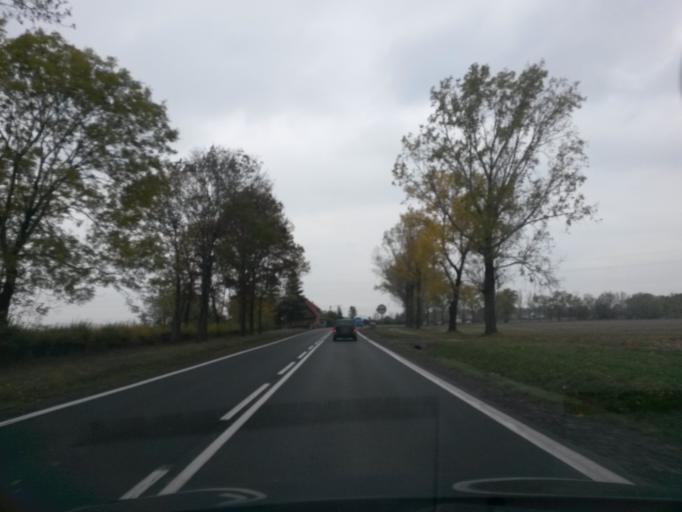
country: PL
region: Lower Silesian Voivodeship
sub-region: Powiat zabkowicki
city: Zabkowice Slaskie
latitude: 50.5654
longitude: 16.7898
